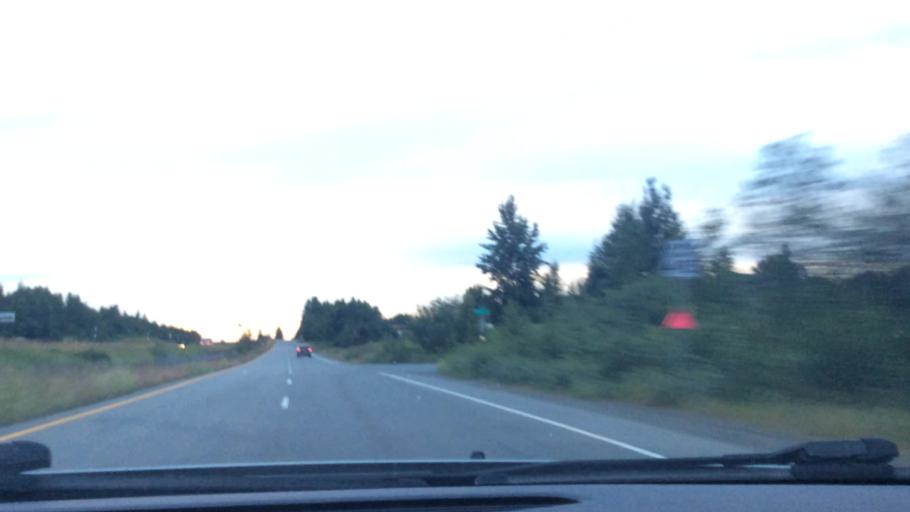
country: US
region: Alaska
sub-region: Anchorage Municipality
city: Anchorage
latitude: 61.1266
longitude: -149.8557
